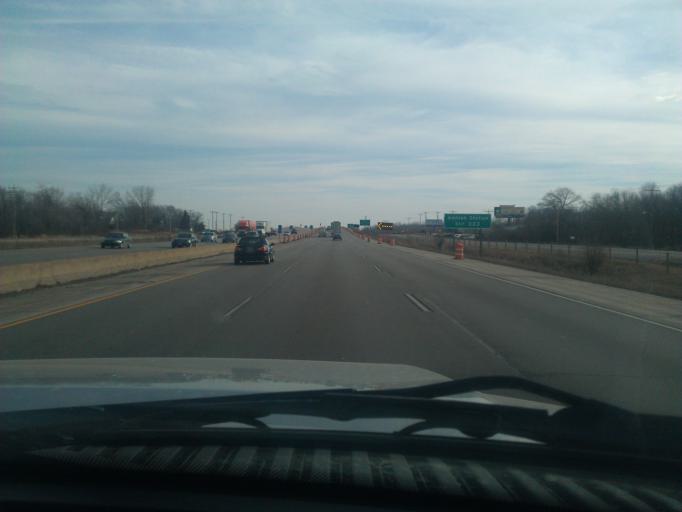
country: US
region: Wisconsin
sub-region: Racine County
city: Franksville
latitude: 42.7477
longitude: -87.9542
